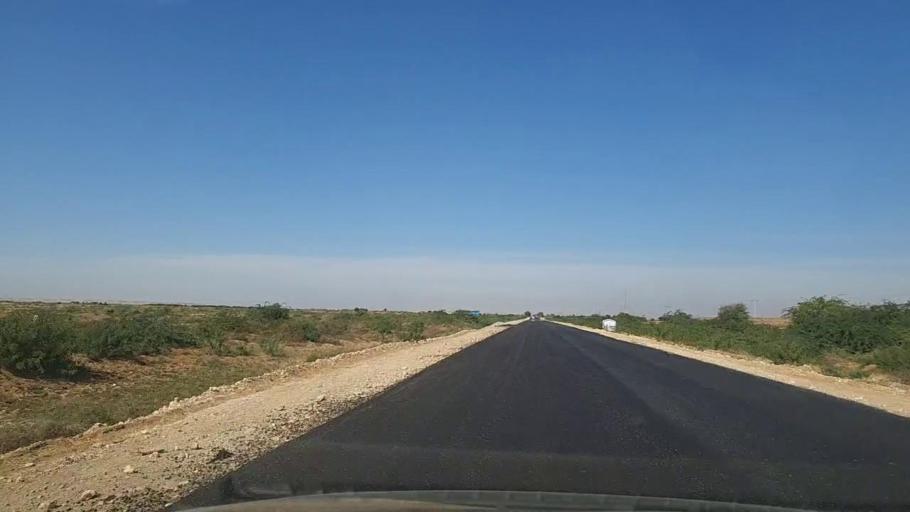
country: PK
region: Sindh
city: Kotri
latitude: 25.2385
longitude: 68.2319
